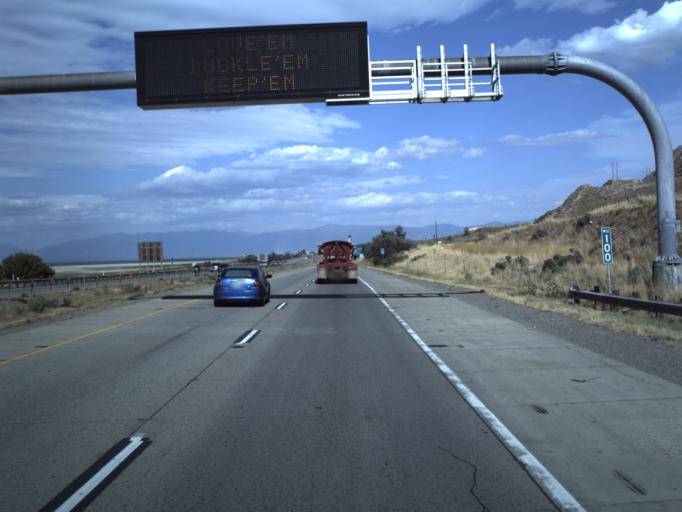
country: US
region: Utah
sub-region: Tooele County
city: Stansbury park
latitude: 40.7093
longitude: -112.2495
